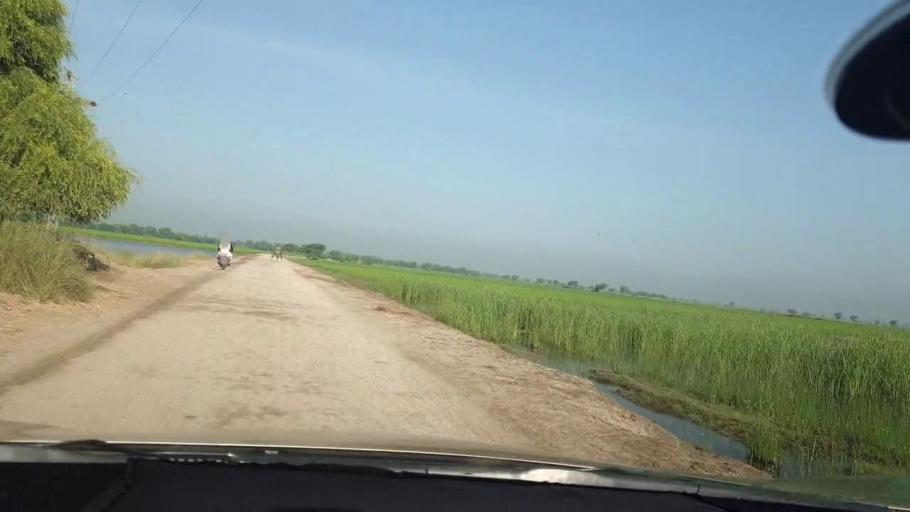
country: PK
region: Sindh
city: Kambar
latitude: 27.6559
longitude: 68.0294
